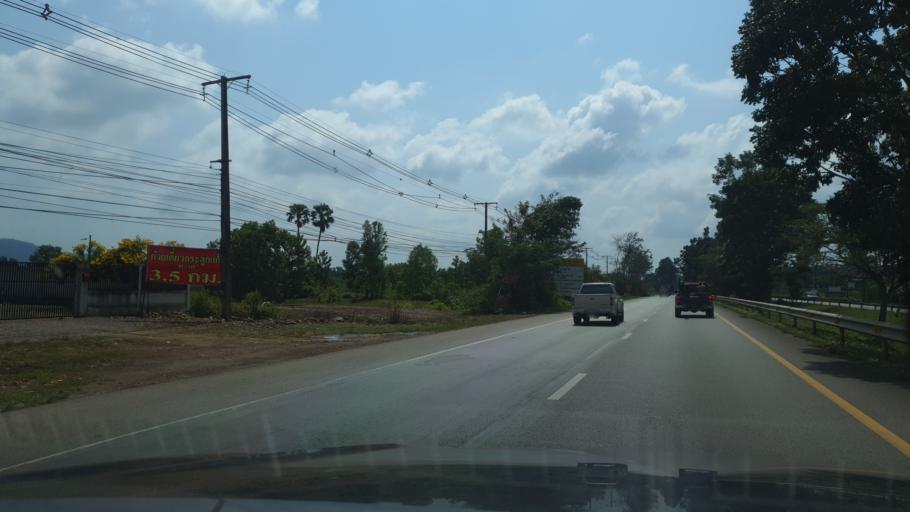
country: TH
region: Chumphon
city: Sawi
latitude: 10.1781
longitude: 99.0966
